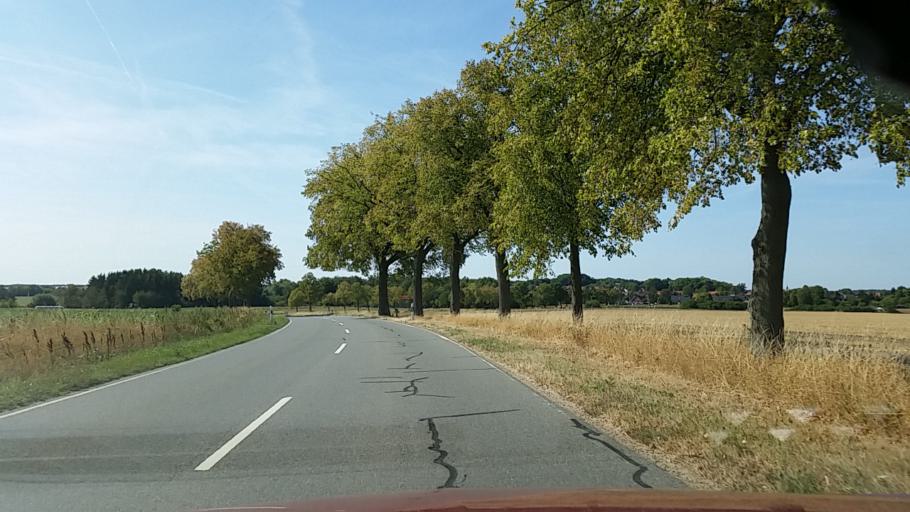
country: DE
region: Lower Saxony
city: Wolfsburg
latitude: 52.4061
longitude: 10.8428
